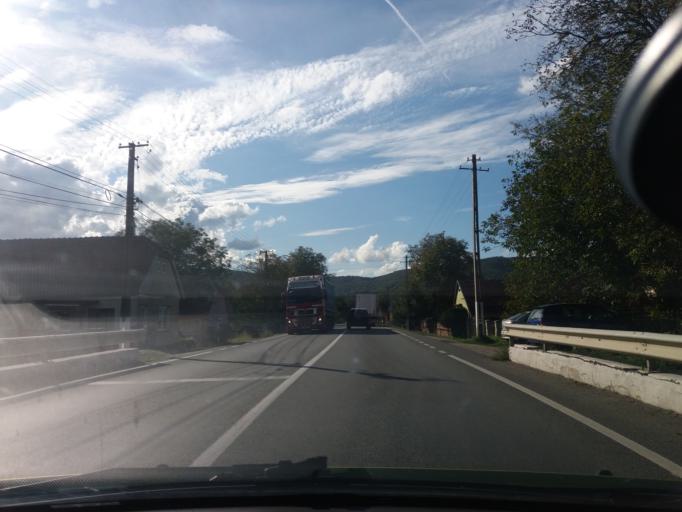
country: RO
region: Arad
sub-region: Comuna Barzava
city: Barzava
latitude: 46.1107
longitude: 21.9753
